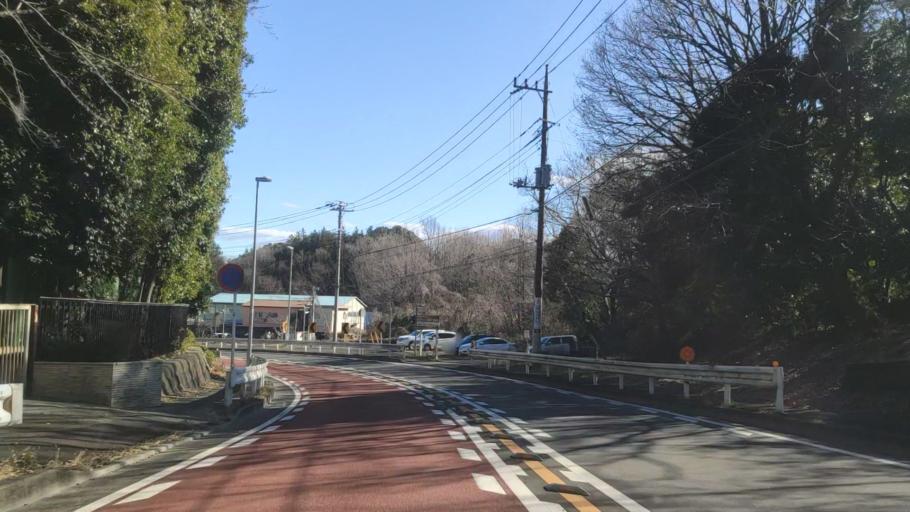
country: JP
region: Kanagawa
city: Minami-rinkan
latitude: 35.5044
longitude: 139.4913
